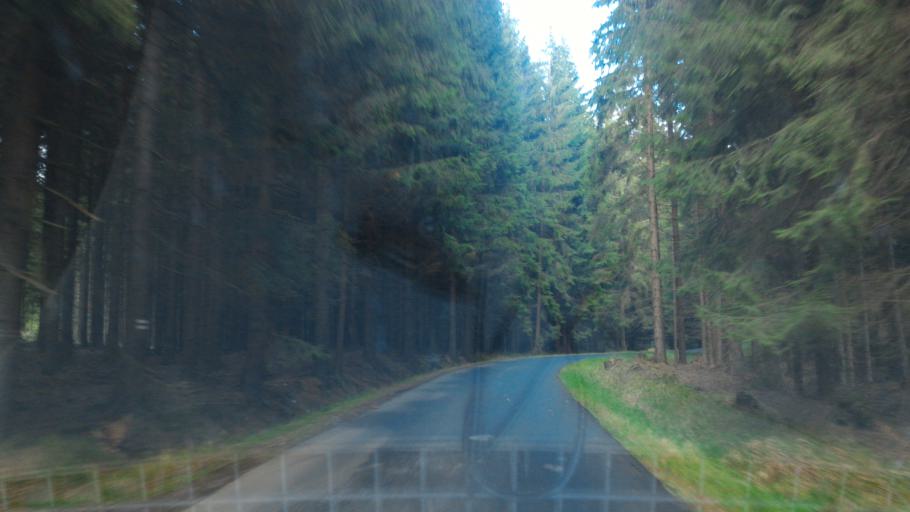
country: CZ
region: Ustecky
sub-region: Okres Decin
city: Chribska
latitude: 50.8184
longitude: 14.4844
